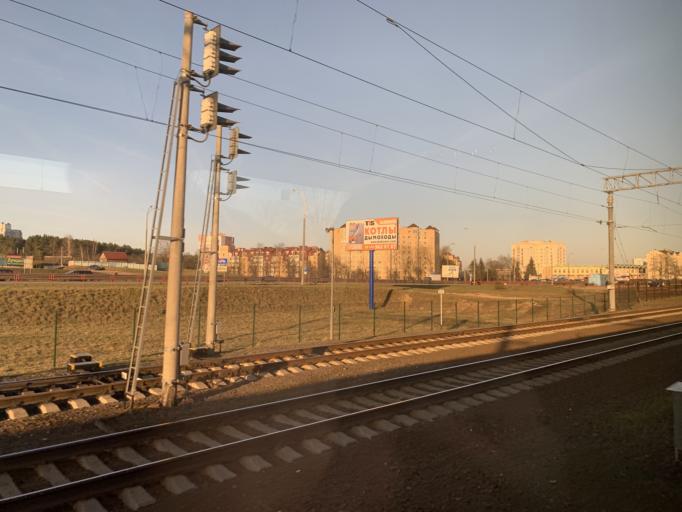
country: BY
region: Minsk
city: Zhdanovichy
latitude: 53.9484
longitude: 27.4226
